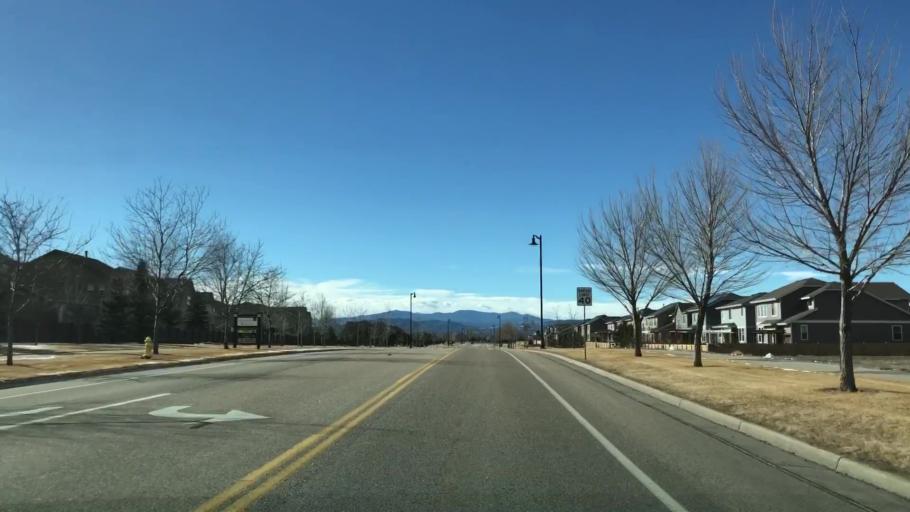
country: US
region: Colorado
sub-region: Weld County
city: Windsor
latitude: 40.5086
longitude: -104.9552
